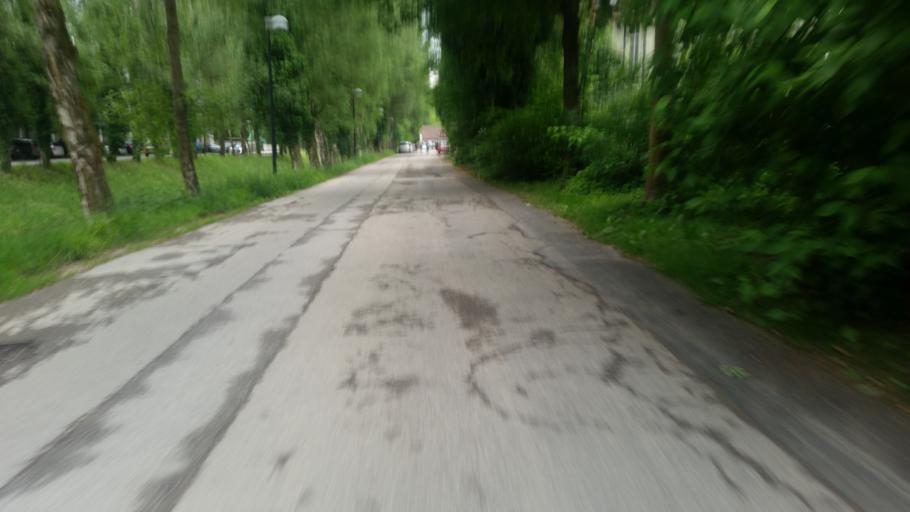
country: AT
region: Salzburg
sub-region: Politischer Bezirk Salzburg-Umgebung
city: Bergheim
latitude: 47.8169
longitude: 13.0263
